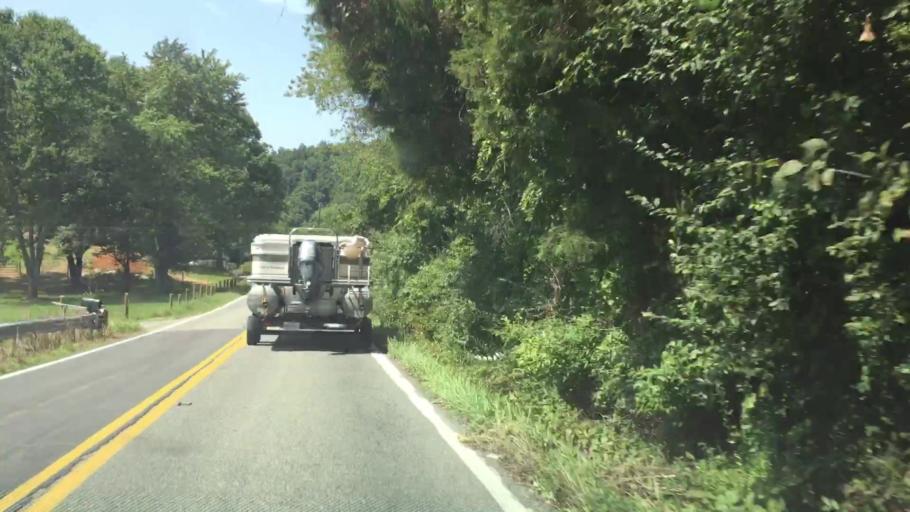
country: US
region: Virginia
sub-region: Washington County
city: Abingdon
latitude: 36.6141
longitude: -82.0220
